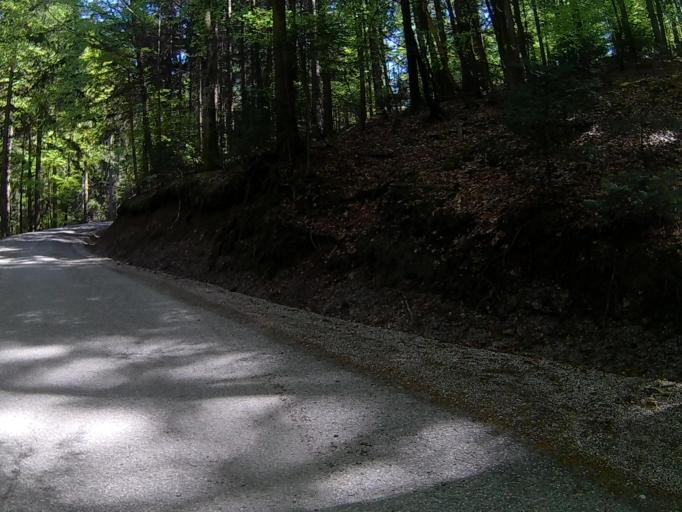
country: SI
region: Ruse
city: Ruse
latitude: 46.5252
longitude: 15.5146
